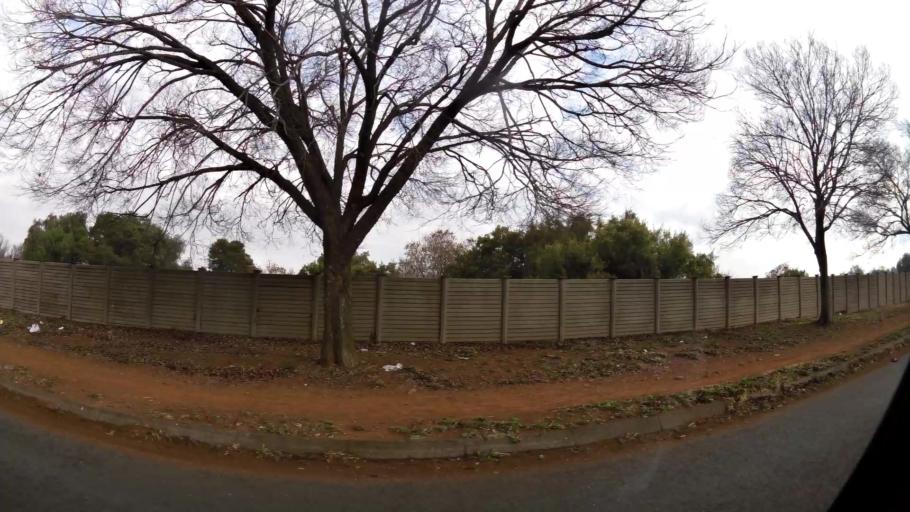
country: ZA
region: Gauteng
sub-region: Sedibeng District Municipality
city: Vanderbijlpark
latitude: -26.6910
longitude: 27.8232
